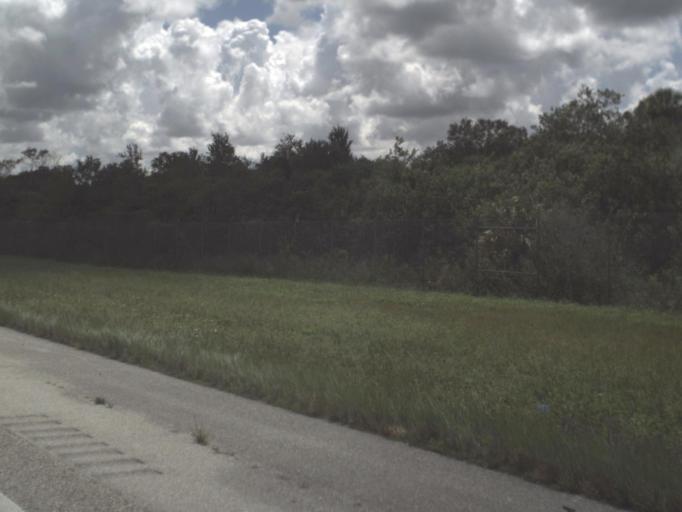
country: US
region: Florida
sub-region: Collier County
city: Orangetree
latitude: 26.1530
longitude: -81.5166
